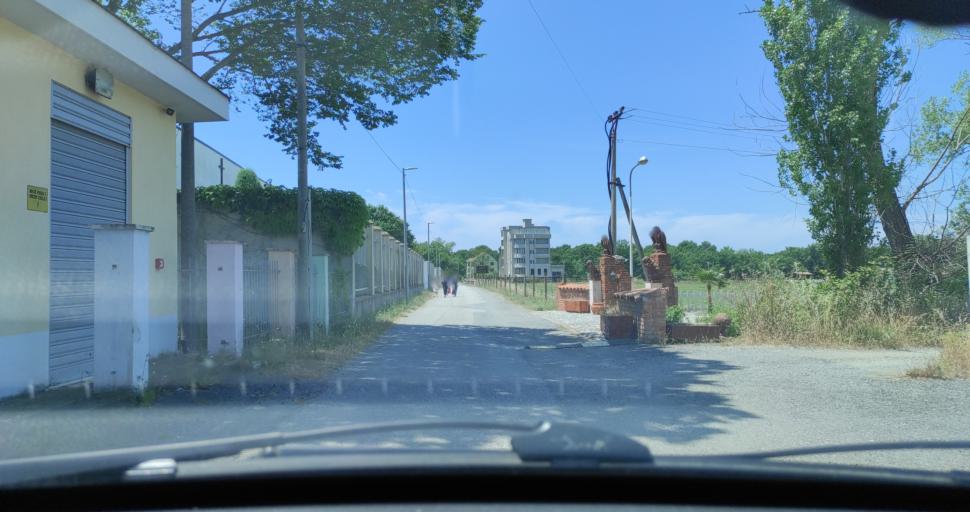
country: AL
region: Shkoder
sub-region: Rrethi i Shkodres
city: Velipoje
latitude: 41.8733
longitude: 19.3994
